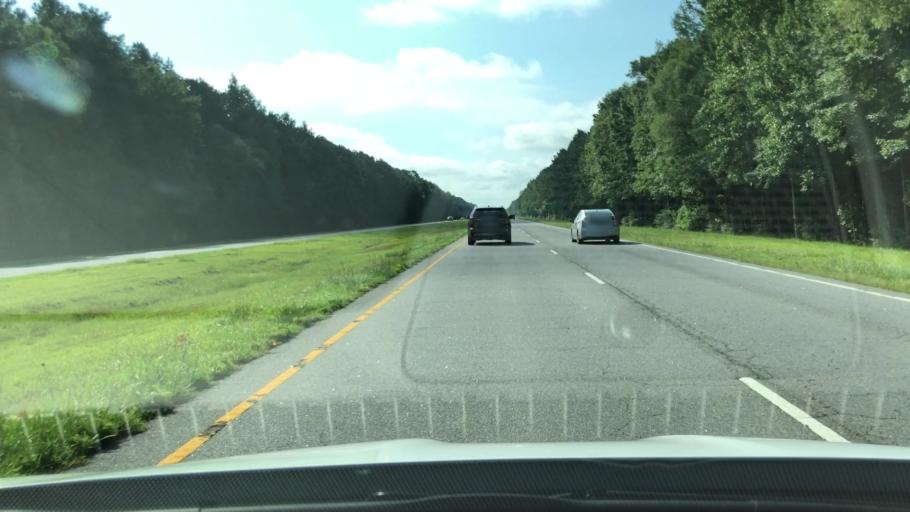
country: US
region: North Carolina
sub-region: Pasquotank County
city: Elizabeth City
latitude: 36.3973
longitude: -76.3290
